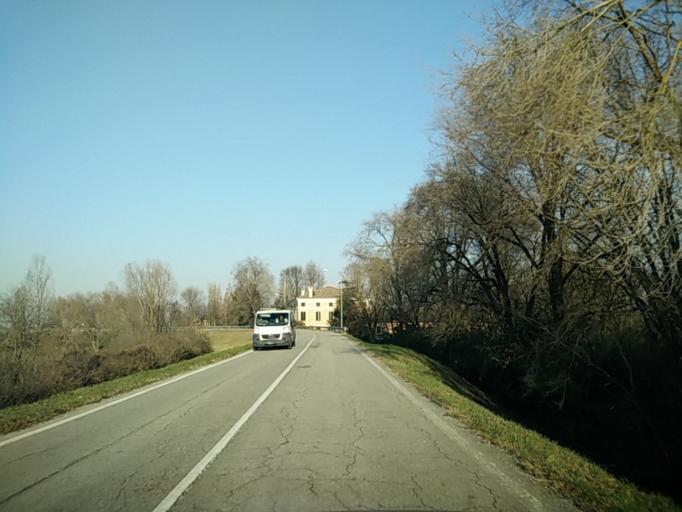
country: IT
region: Veneto
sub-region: Provincia di Venezia
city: Torre di Mosto
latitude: 45.7004
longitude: 12.7101
